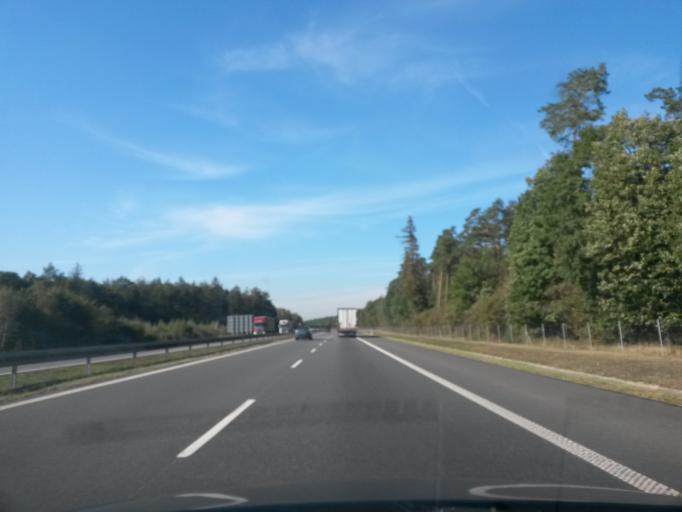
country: PL
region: Opole Voivodeship
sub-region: Powiat opolski
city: Proszkow
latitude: 50.5430
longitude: 17.8983
